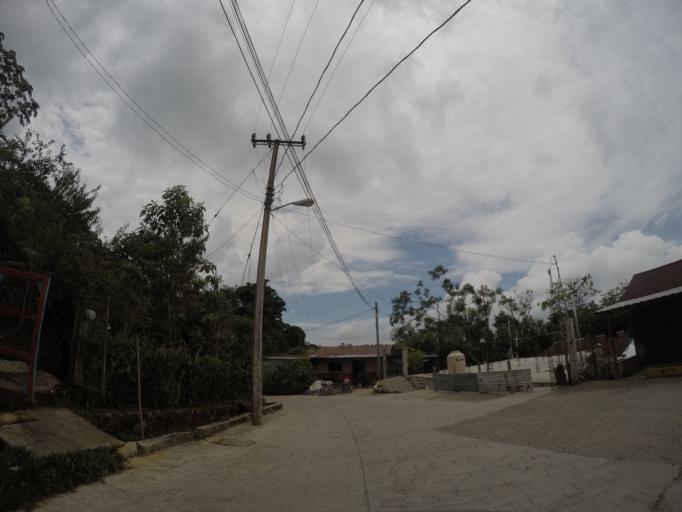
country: MX
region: Oaxaca
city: Pluma Hidalgo
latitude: 15.9244
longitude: -96.4186
